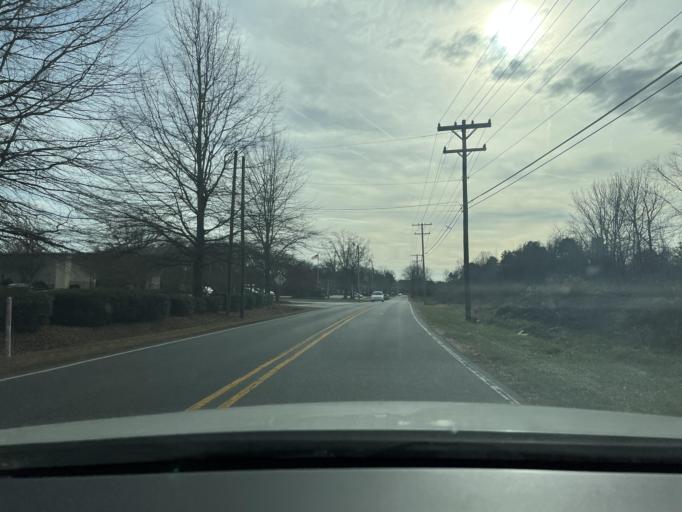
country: US
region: North Carolina
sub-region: Guilford County
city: Pleasant Garden
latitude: 36.0132
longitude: -79.7762
